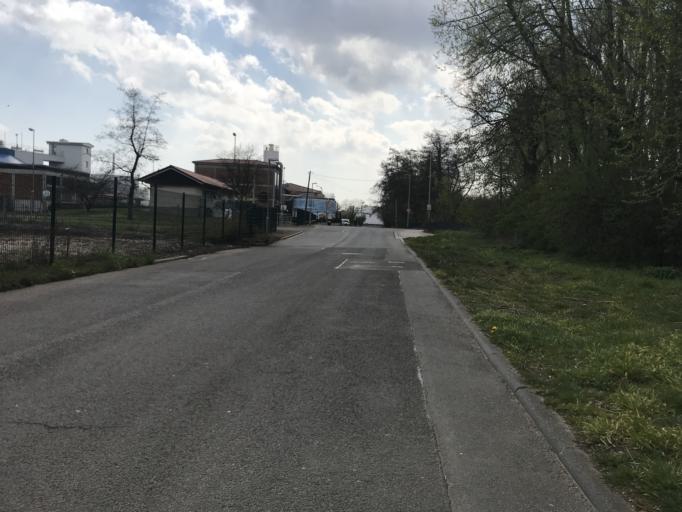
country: DE
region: Hesse
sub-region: Regierungsbezirk Darmstadt
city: Russelsheim
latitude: 50.0016
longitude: 8.4026
